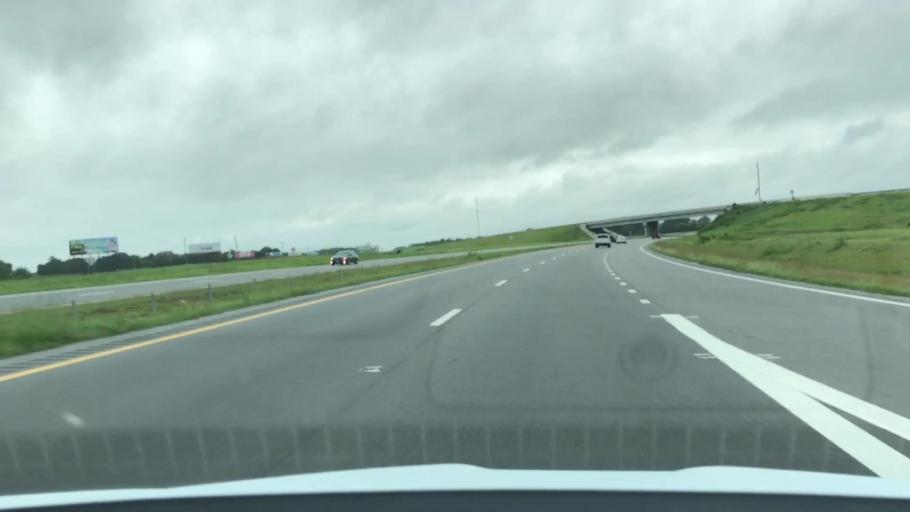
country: US
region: North Carolina
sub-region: Lenoir County
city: La Grange
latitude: 35.3017
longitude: -77.8165
